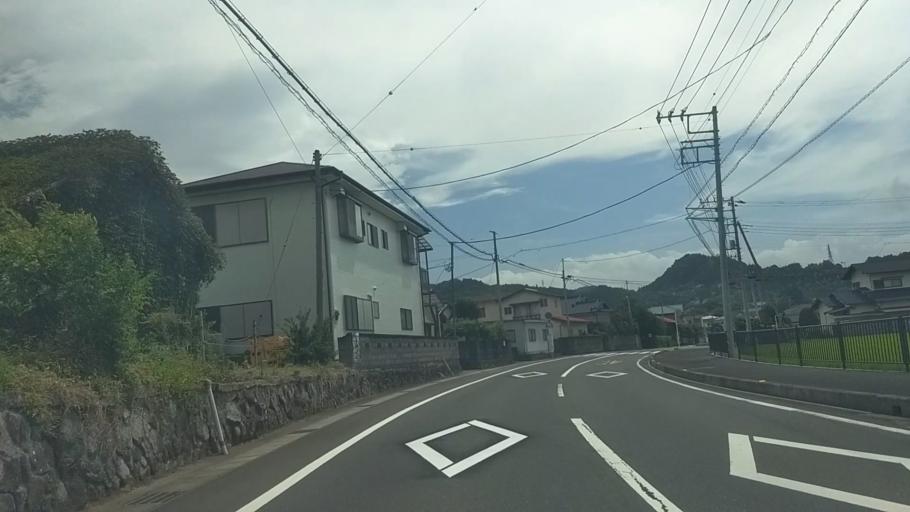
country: JP
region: Shizuoka
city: Mishima
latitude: 35.0406
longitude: 138.9582
